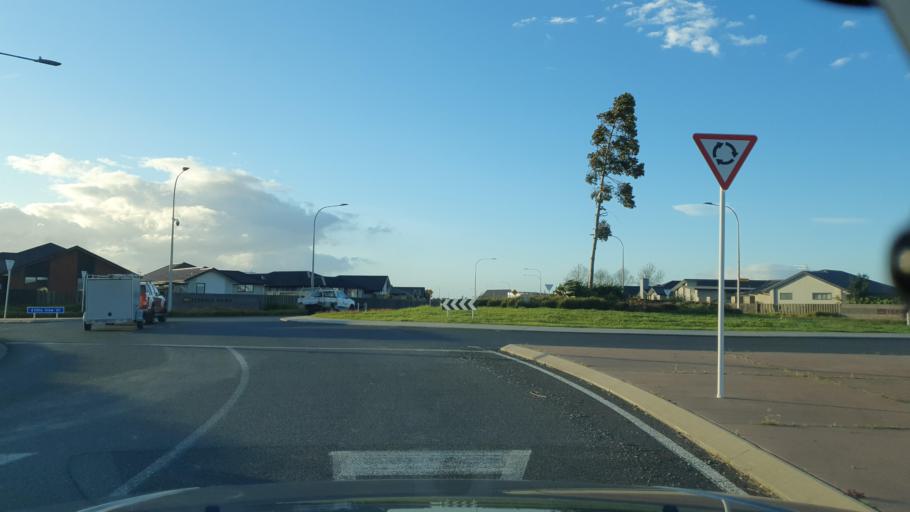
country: NZ
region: Bay of Plenty
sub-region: Western Bay of Plenty District
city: Maketu
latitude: -37.7194
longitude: 176.3151
